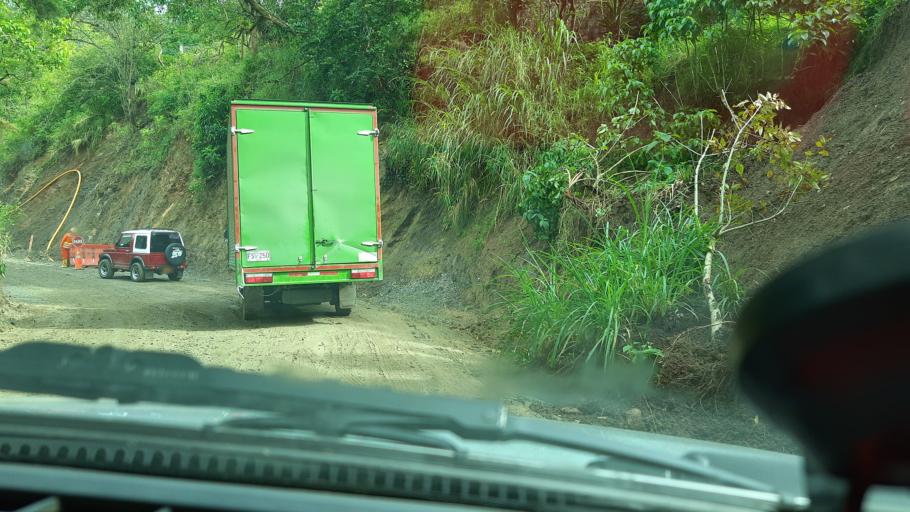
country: CO
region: Cundinamarca
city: Tenza
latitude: 5.0762
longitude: -73.3953
